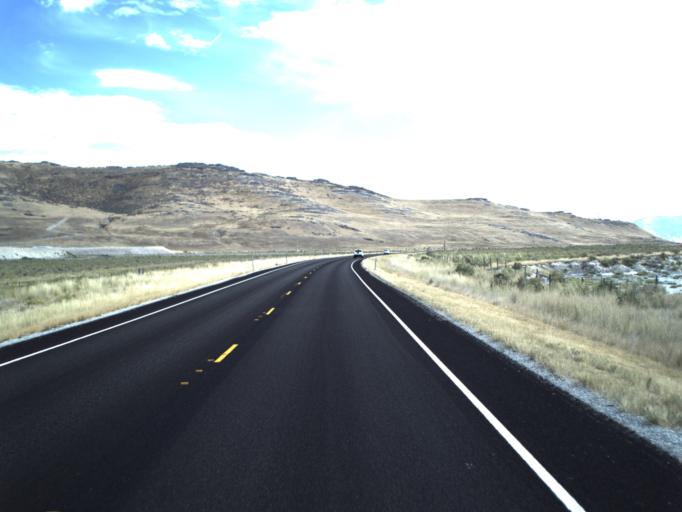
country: US
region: Utah
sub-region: Box Elder County
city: Tremonton
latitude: 41.6275
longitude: -112.4019
